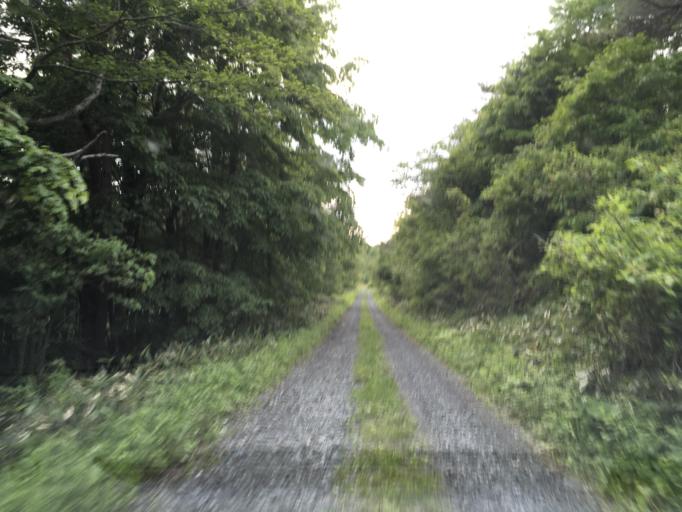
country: JP
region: Iwate
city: Mizusawa
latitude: 39.1311
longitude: 141.3214
